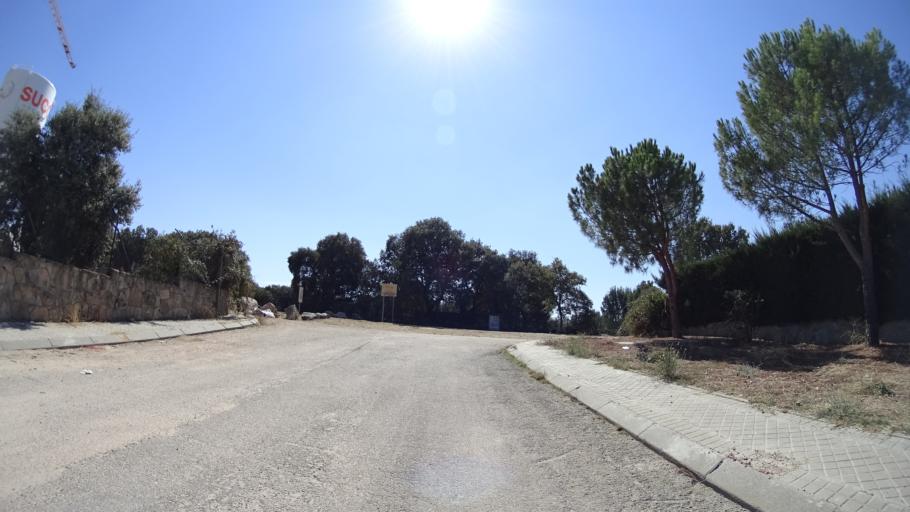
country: ES
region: Madrid
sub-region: Provincia de Madrid
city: Collado-Villalba
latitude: 40.6135
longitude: -4.0171
